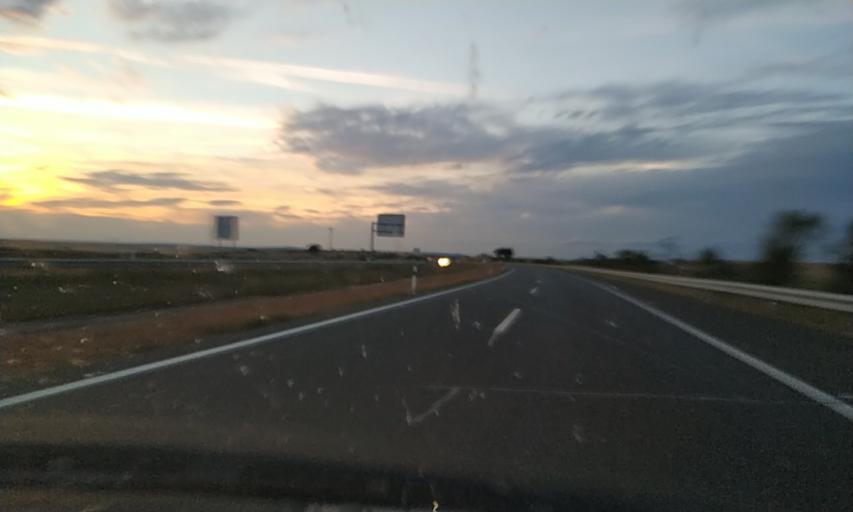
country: ES
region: Extremadura
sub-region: Provincia de Caceres
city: Caceres
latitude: 39.4712
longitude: -6.4255
